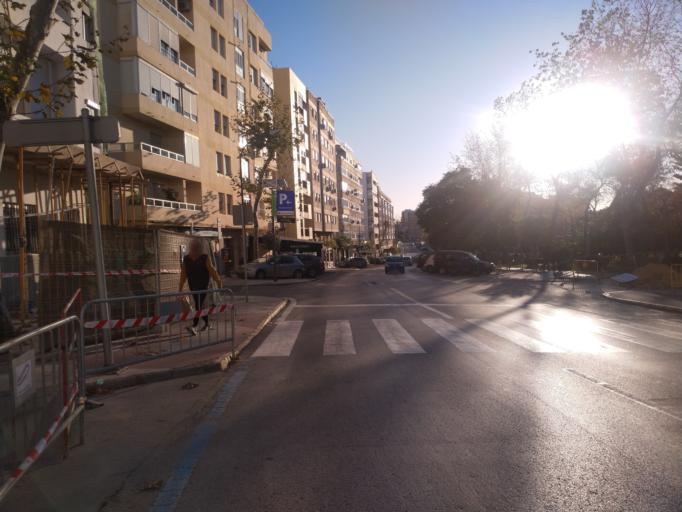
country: ES
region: Andalusia
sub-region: Provincia de Cadiz
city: San Fernando
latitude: 36.4664
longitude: -6.2001
